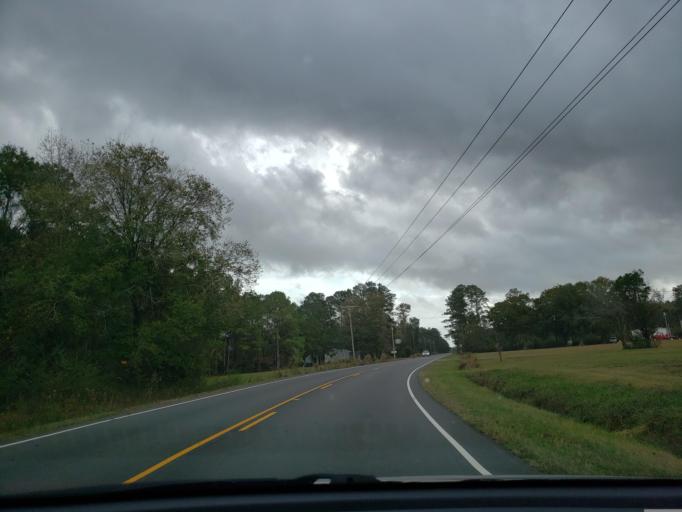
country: US
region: North Carolina
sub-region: Duplin County
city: Kenansville
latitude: 34.8682
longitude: -77.8846
